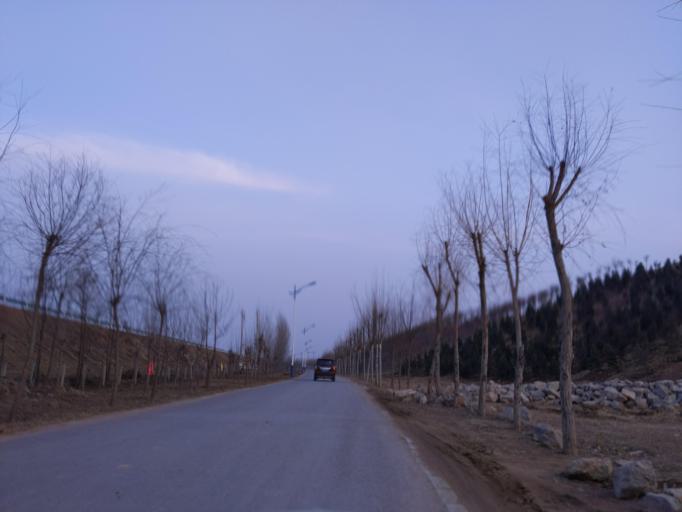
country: CN
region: Henan Sheng
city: Zhongyuanlu
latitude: 35.8156
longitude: 115.0604
